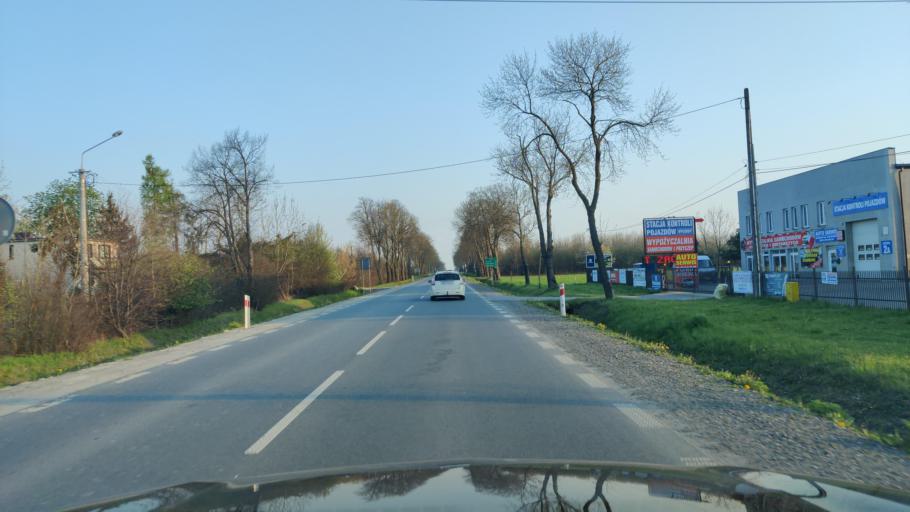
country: PL
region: Masovian Voivodeship
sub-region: Powiat pultuski
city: Pultusk
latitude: 52.6863
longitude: 21.0806
